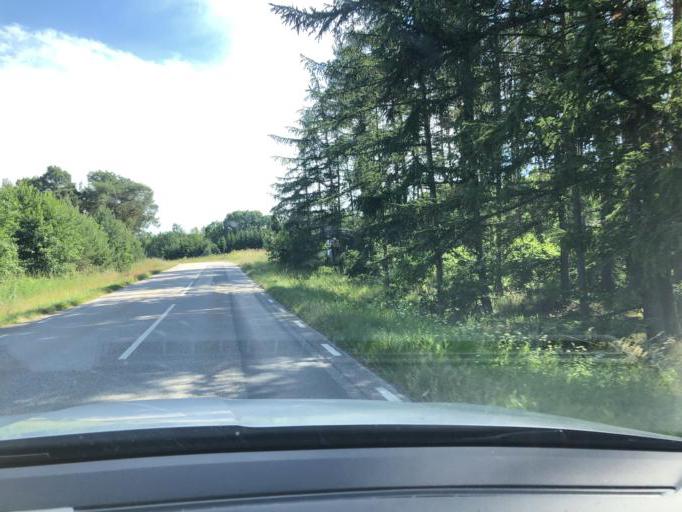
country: SE
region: Blekinge
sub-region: Solvesborgs Kommun
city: Soelvesborg
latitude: 56.0781
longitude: 14.6085
